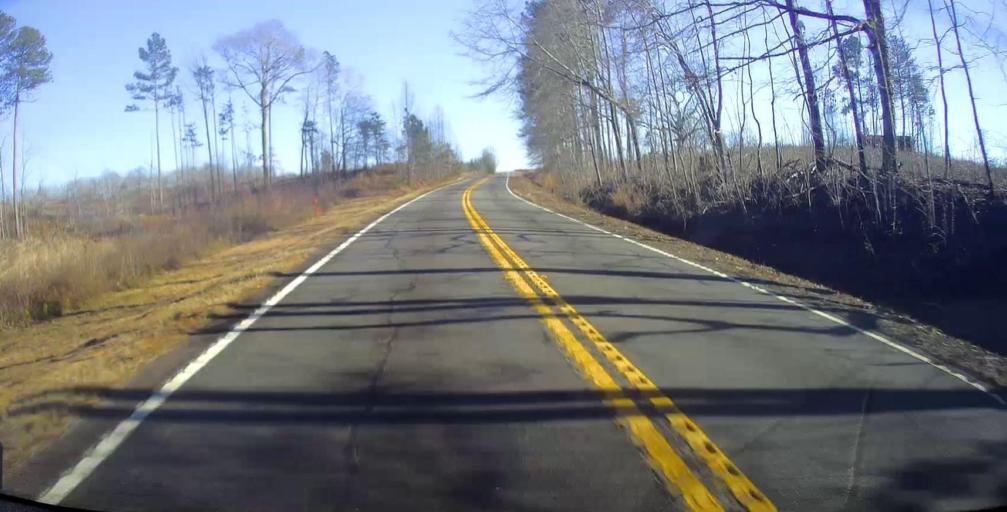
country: US
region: Georgia
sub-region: Talbot County
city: Talbotton
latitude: 32.6680
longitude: -84.4659
